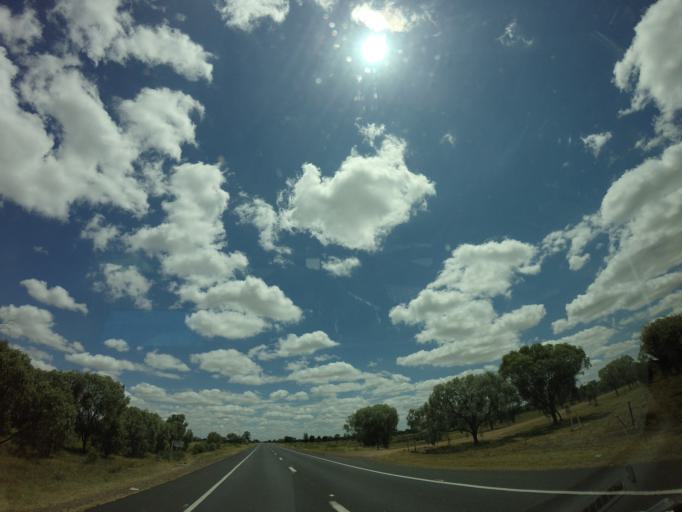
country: AU
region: New South Wales
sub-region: Moree Plains
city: Moree
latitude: -29.1023
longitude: 150.0319
